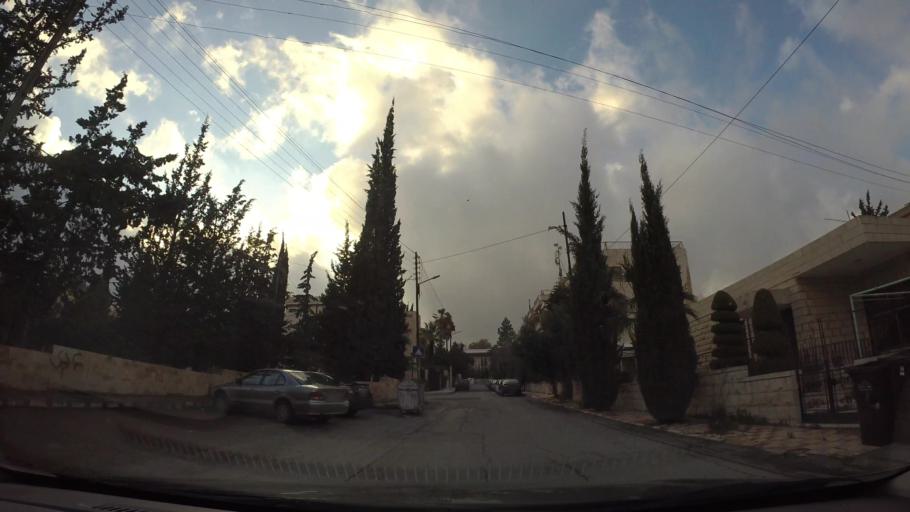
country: JO
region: Amman
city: Amman
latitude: 31.9559
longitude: 35.8931
